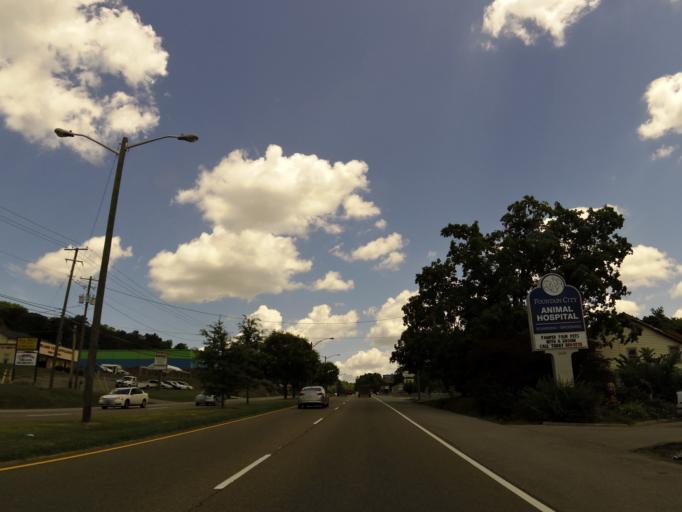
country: US
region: Tennessee
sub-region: Knox County
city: Knoxville
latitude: 36.0469
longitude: -83.9285
